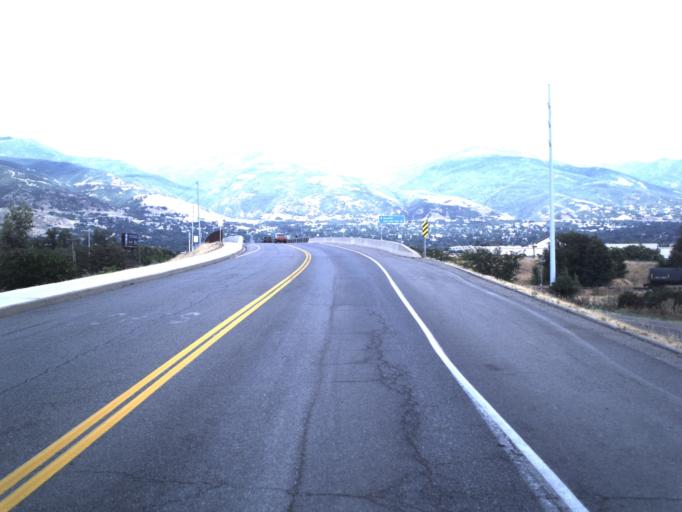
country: US
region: Utah
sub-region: Davis County
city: West Bountiful
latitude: 40.8938
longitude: -111.8989
